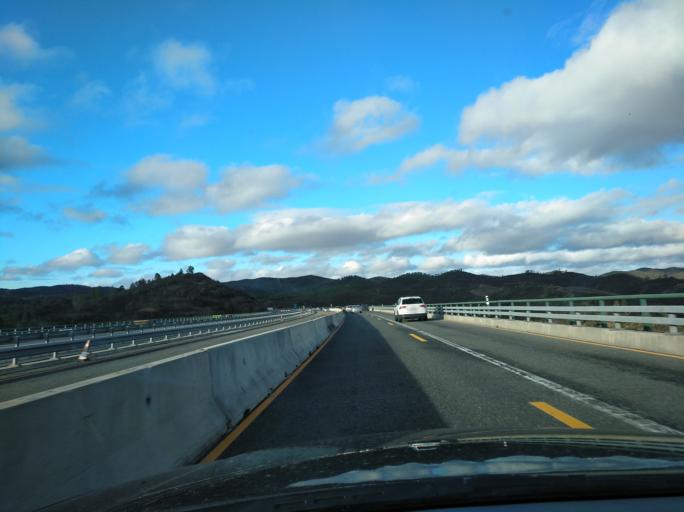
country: PT
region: Faro
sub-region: Silves
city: Sao Bartolomeu de Messines
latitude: 37.3060
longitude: -8.2542
